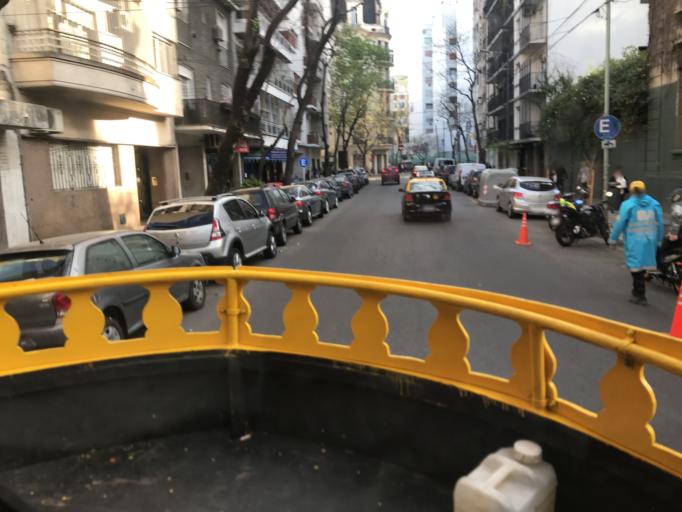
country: AR
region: Buenos Aires F.D.
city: Retiro
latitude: -34.5925
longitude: -58.4079
